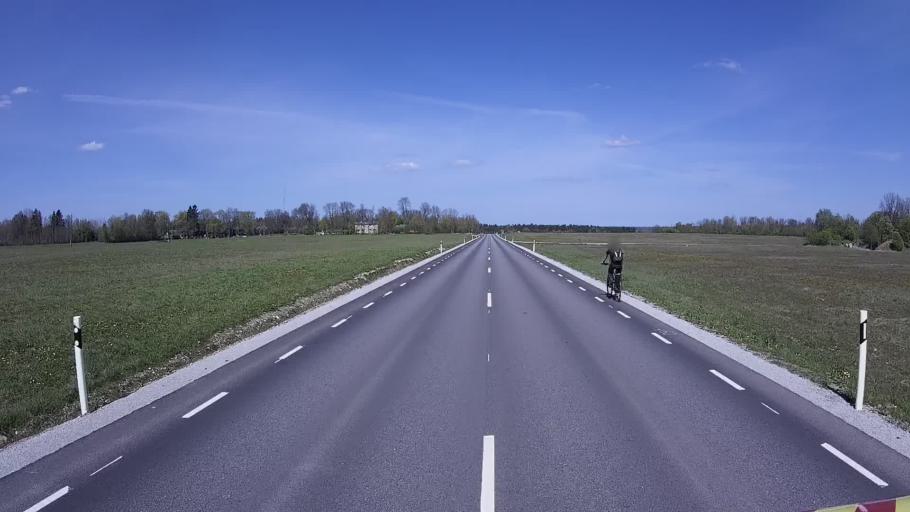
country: EE
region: Harju
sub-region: Paldiski linn
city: Paldiski
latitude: 59.2068
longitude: 24.0955
